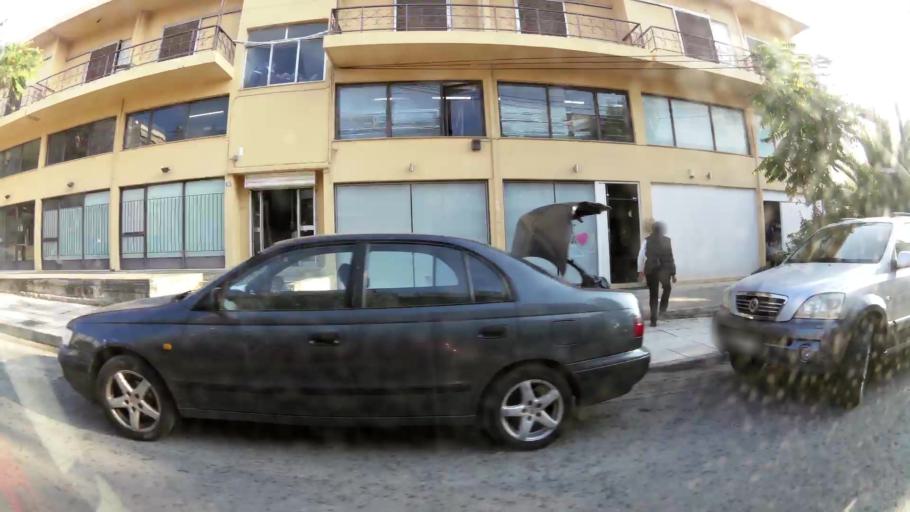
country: GR
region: Attica
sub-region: Nomarchia Athinas
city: Nea Filadelfeia
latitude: 38.0441
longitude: 23.7322
